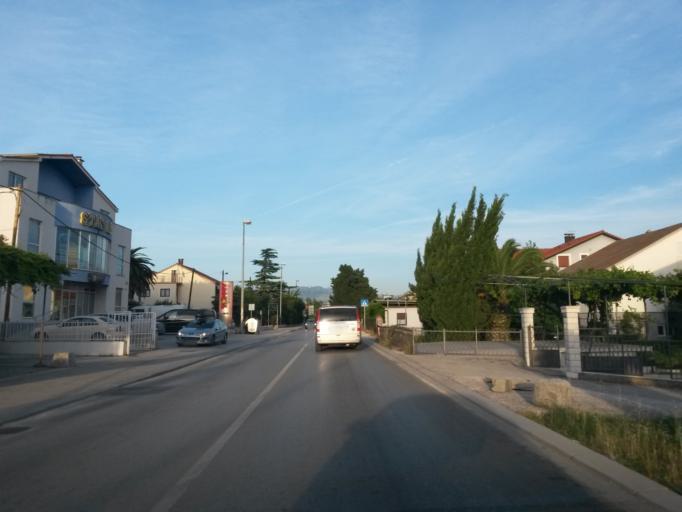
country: HR
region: Splitsko-Dalmatinska
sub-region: Grad Split
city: Split
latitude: 43.5533
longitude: 16.3687
